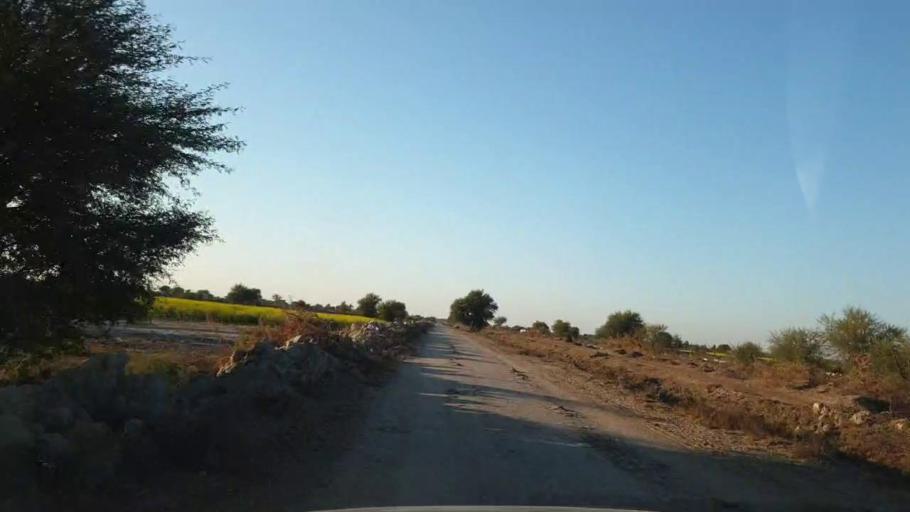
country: PK
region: Sindh
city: Jhol
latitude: 25.8848
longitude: 68.8991
